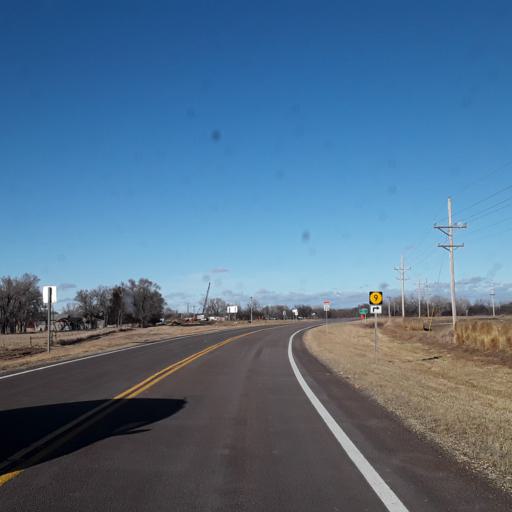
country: US
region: Kansas
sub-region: Cloud County
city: Concordia
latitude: 39.5711
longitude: -97.7062
